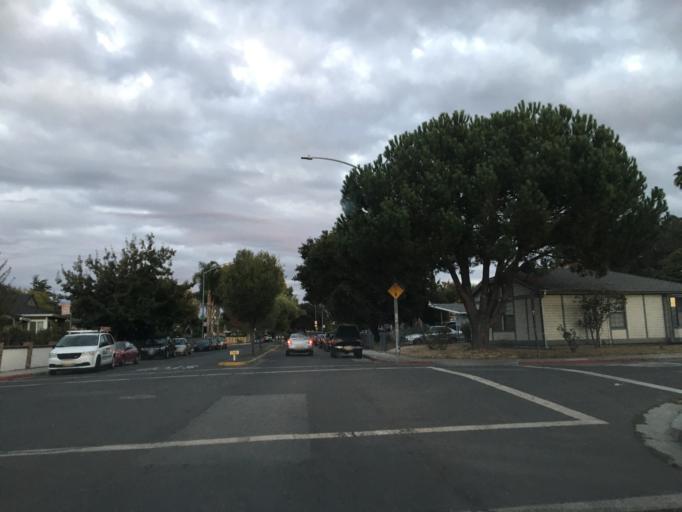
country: US
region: California
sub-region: San Mateo County
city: East Palo Alto
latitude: 37.4713
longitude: -122.1501
